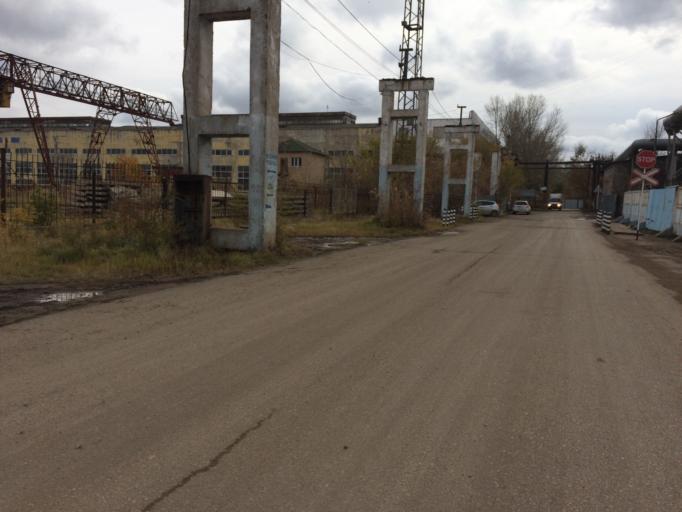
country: KZ
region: Astana Qalasy
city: Astana
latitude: 51.1832
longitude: 71.4316
